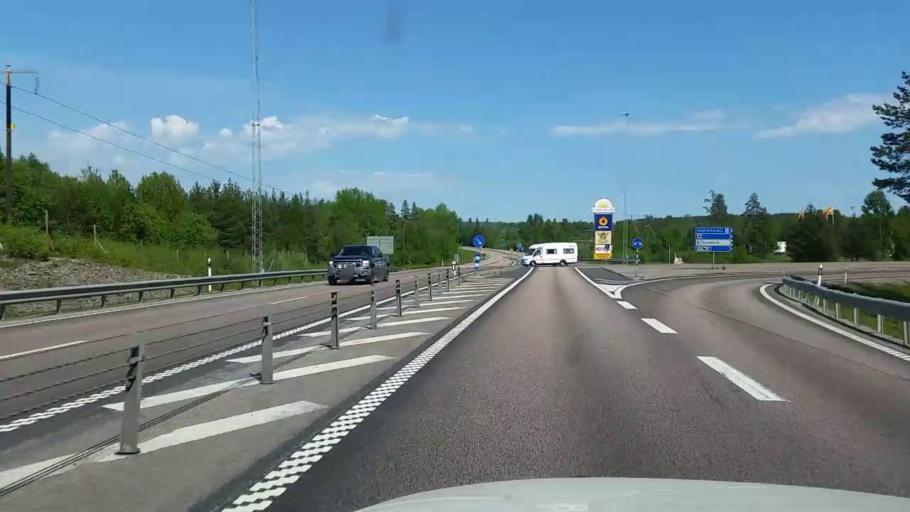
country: SE
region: Gaevleborg
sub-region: Hudiksvalls Kommun
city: Hudiksvall
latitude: 61.7418
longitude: 17.0752
